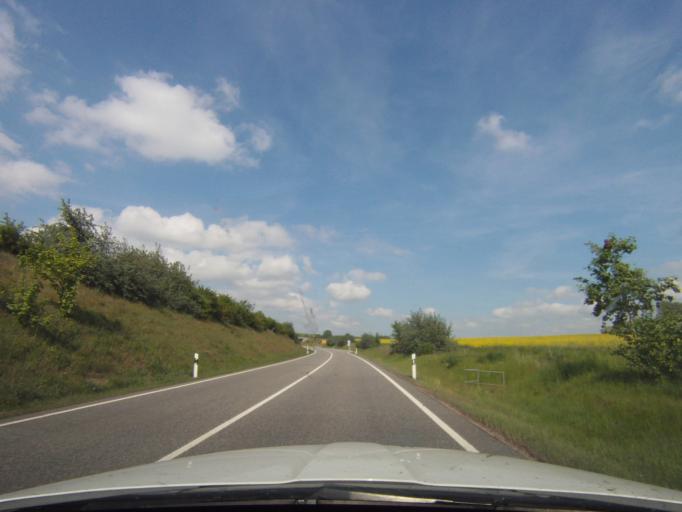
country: DE
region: Thuringia
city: Miesitz
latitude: 50.7369
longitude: 11.8357
